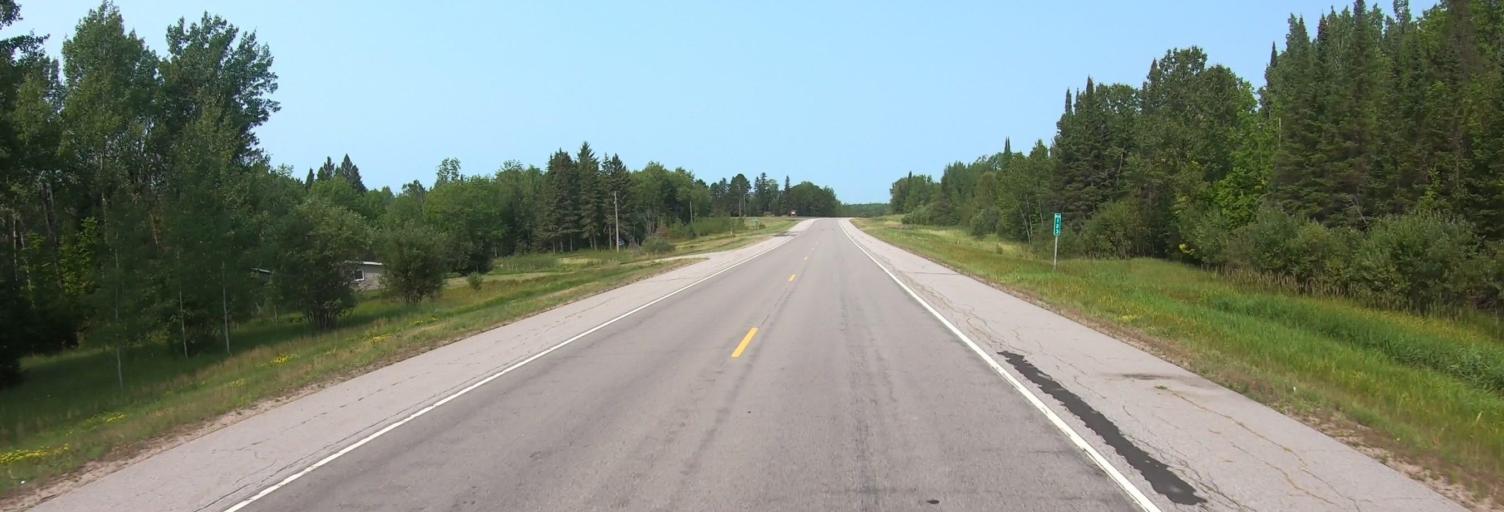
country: CA
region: Ontario
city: Fort Frances
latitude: 48.2175
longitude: -92.9115
